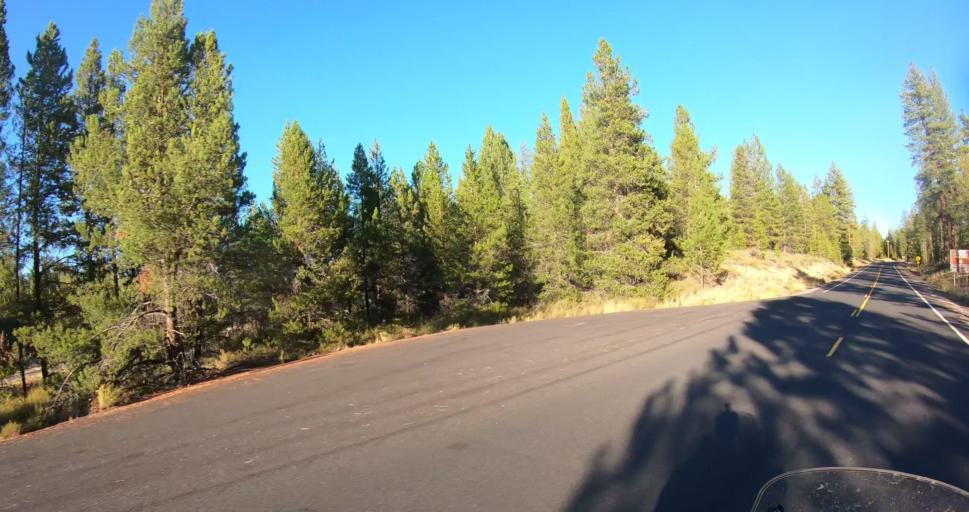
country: US
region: Oregon
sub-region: Deschutes County
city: La Pine
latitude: 43.7271
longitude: -121.4234
